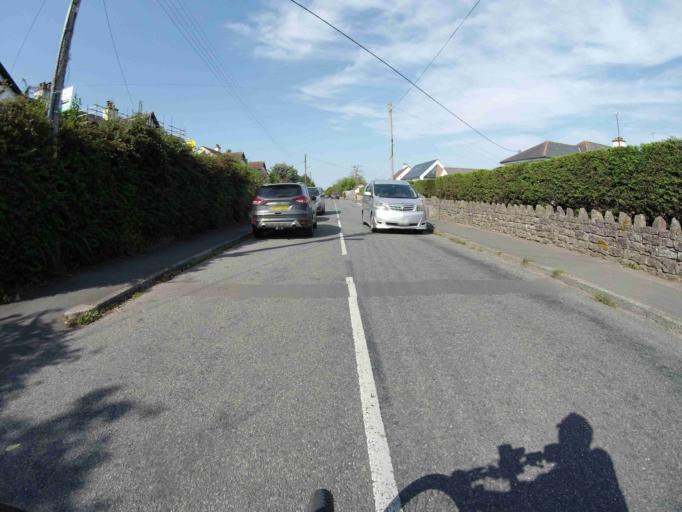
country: GB
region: England
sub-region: Devon
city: Budleigh Salterton
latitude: 50.6370
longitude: -3.3184
